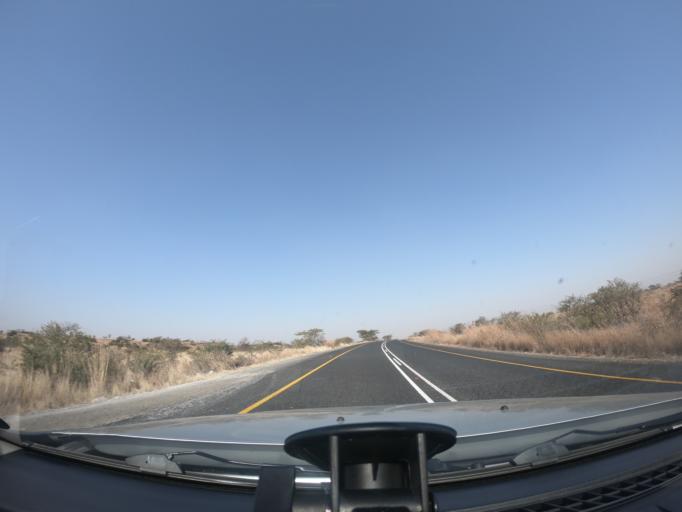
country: ZA
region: KwaZulu-Natal
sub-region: uThukela District Municipality
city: Ladysmith
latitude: -28.7154
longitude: 29.8161
